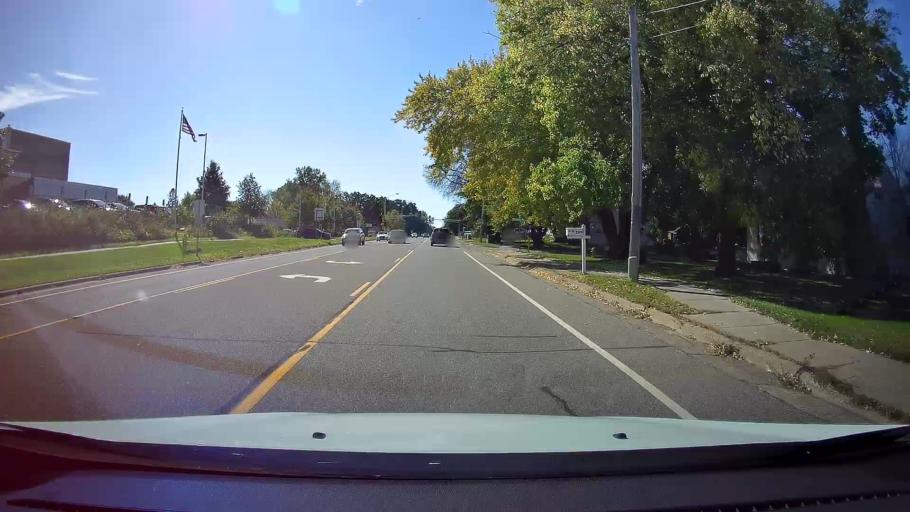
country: US
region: Minnesota
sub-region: Ramsey County
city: Roseville
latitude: 45.0078
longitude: -93.1567
